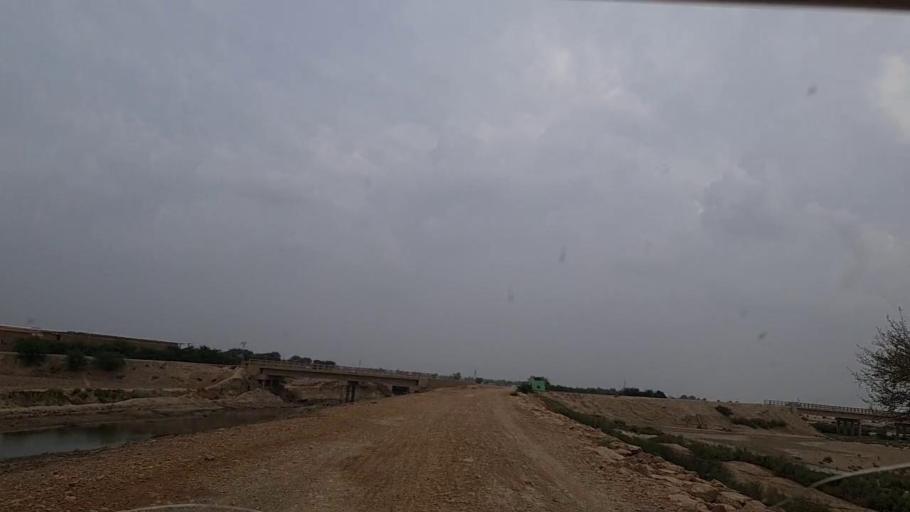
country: PK
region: Sindh
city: Johi
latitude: 26.6989
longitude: 67.5989
